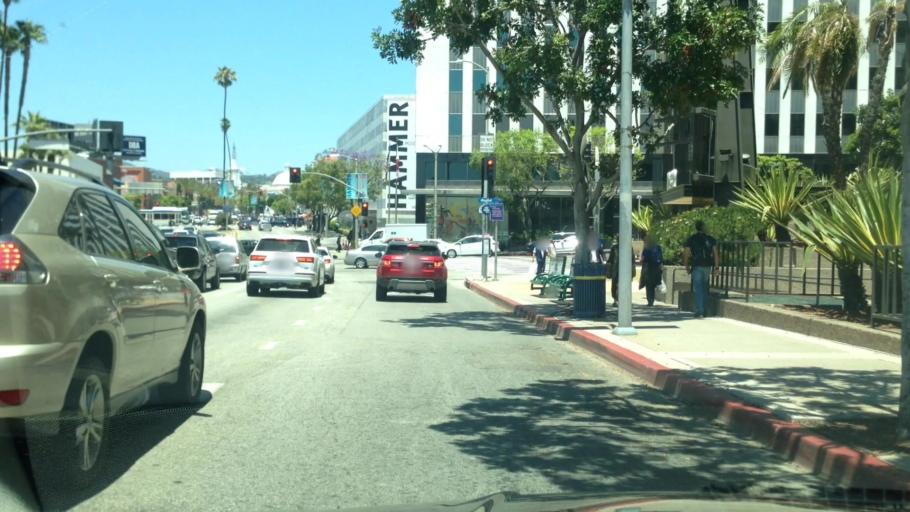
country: US
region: California
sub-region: Los Angeles County
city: Westwood, Los Angeles
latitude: 34.0583
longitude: -118.4435
